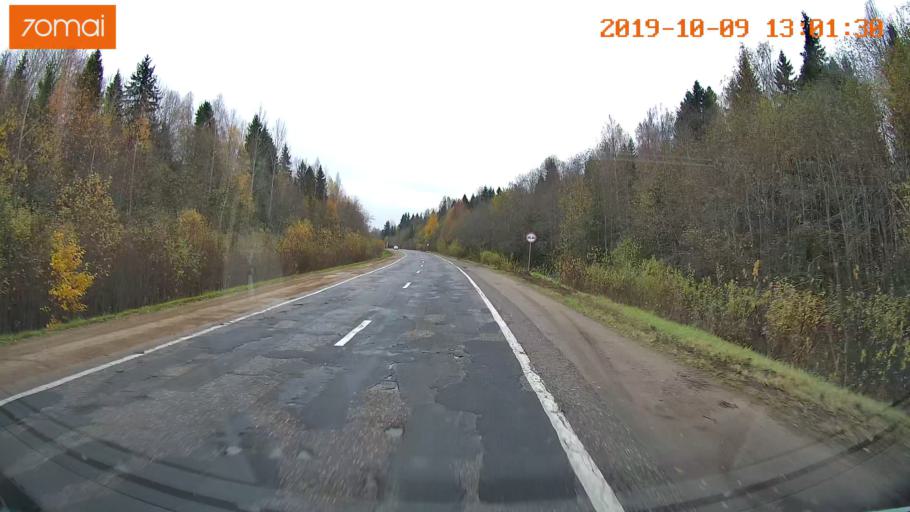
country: RU
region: Jaroslavl
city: Prechistoye
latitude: 58.3677
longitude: 40.4872
